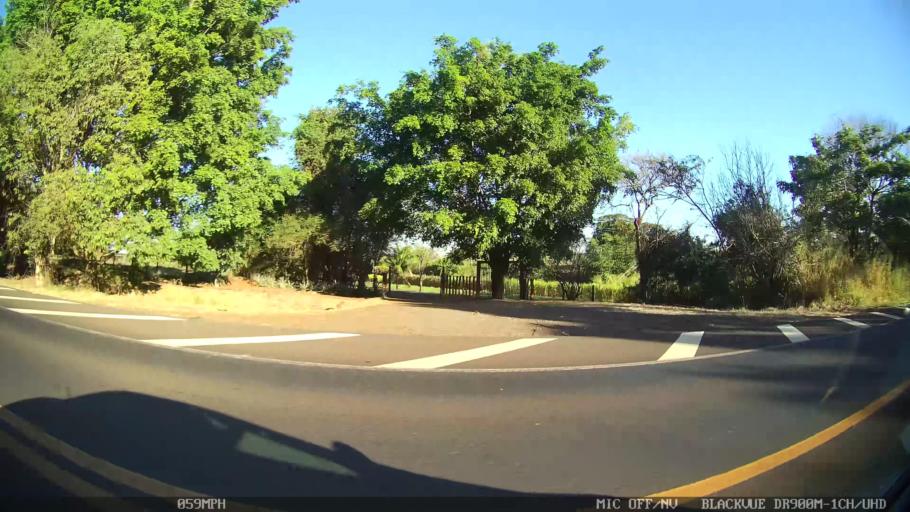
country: BR
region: Sao Paulo
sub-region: Guapiacu
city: Guapiacu
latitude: -20.7629
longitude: -49.1849
